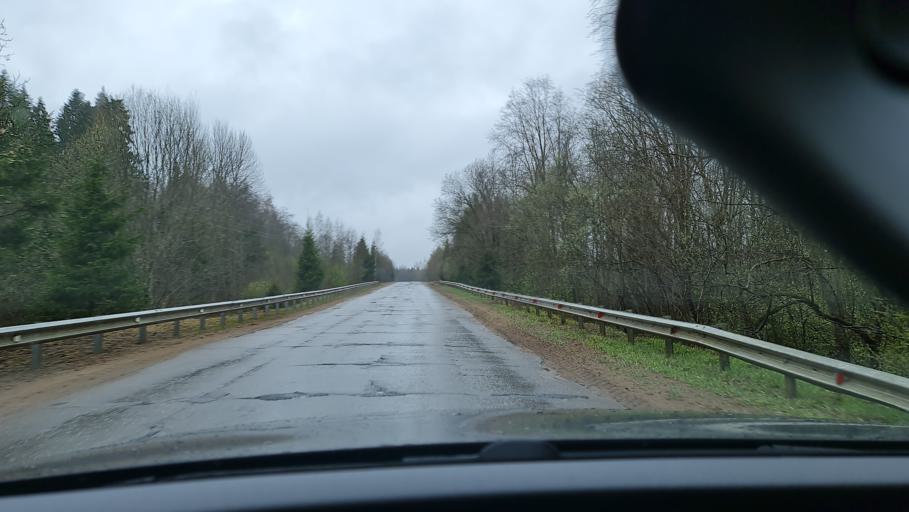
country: RU
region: Novgorod
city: Kresttsy
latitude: 58.0346
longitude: 32.8390
